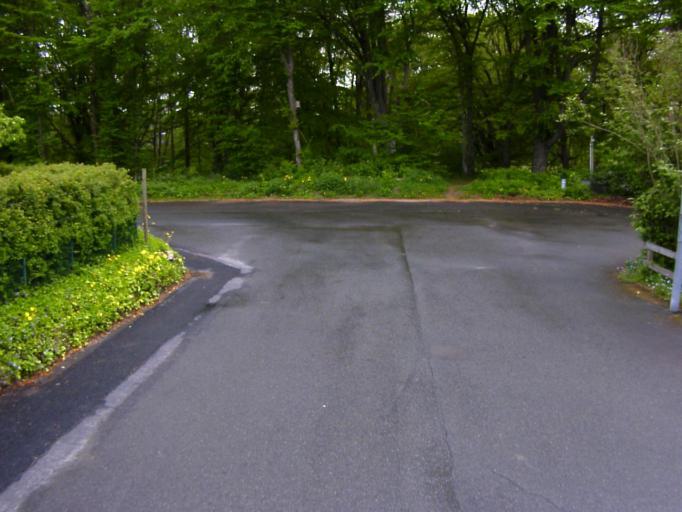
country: SE
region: Skane
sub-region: Kristianstads Kommun
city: Degeberga
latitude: 55.8278
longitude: 14.0811
